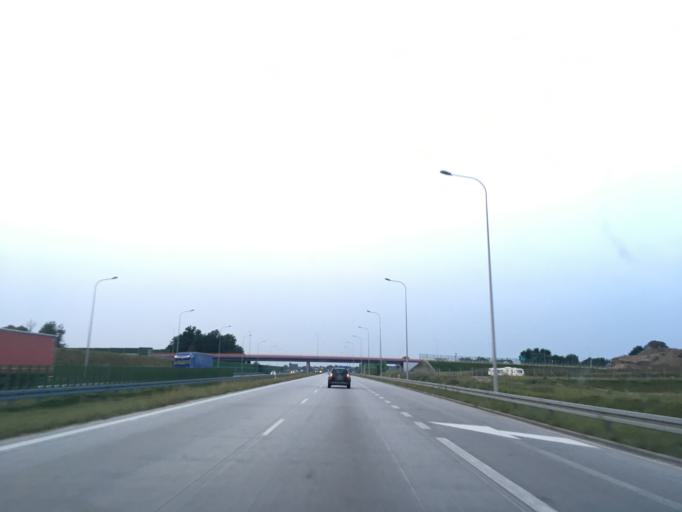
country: PL
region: Lodz Voivodeship
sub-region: Powiat lodzki wschodni
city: Andrespol
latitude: 51.7951
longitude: 19.6187
